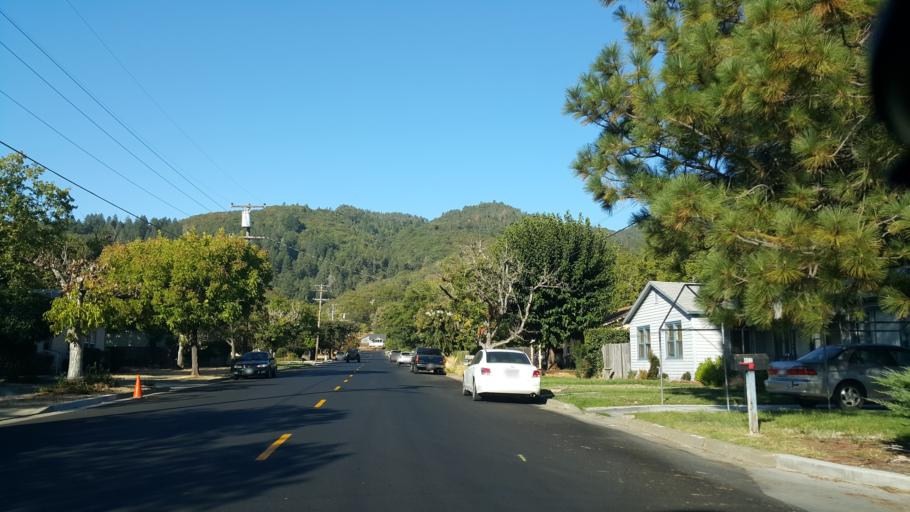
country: US
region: California
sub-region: Mendocino County
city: Ukiah
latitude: 39.1371
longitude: -123.2107
